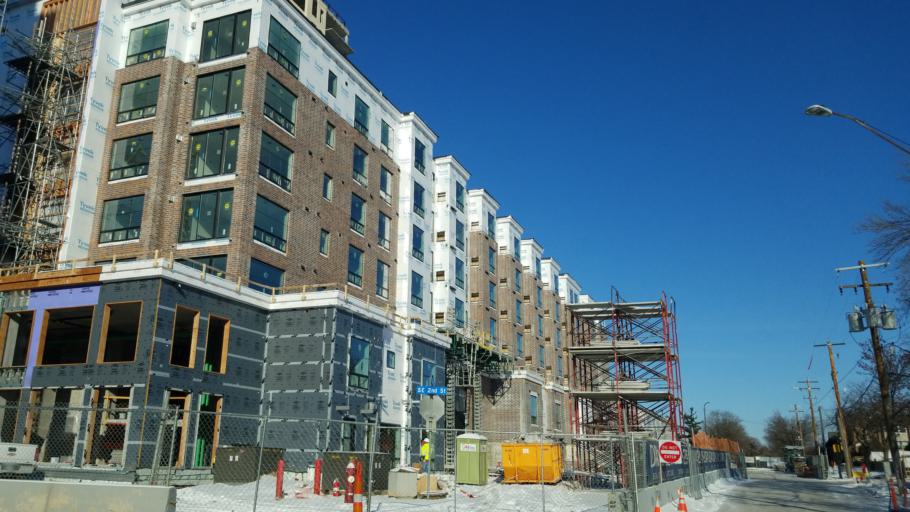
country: US
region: Minnesota
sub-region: Hennepin County
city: Minneapolis
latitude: 44.9847
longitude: -93.2529
